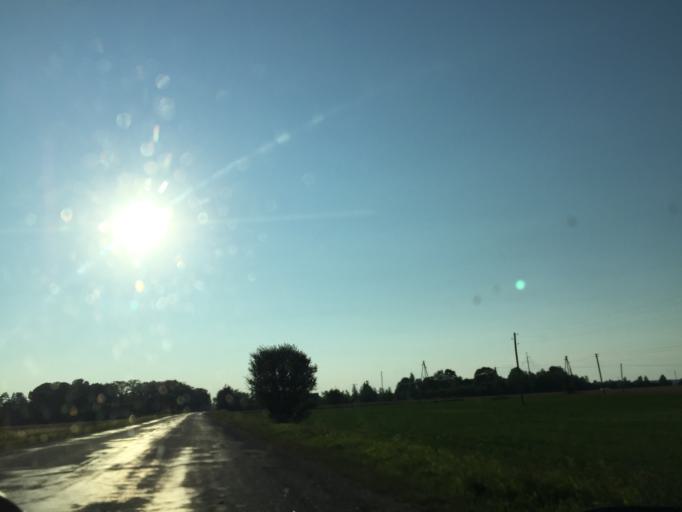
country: LV
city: Tervete
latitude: 56.4409
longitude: 23.4867
